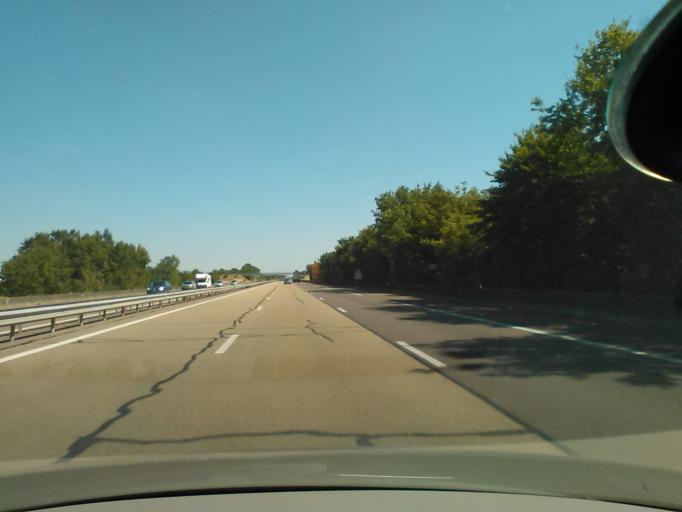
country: FR
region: Bourgogne
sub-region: Departement de l'Yonne
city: Saint-Julien-du-Sault
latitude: 47.9686
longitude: 3.2056
